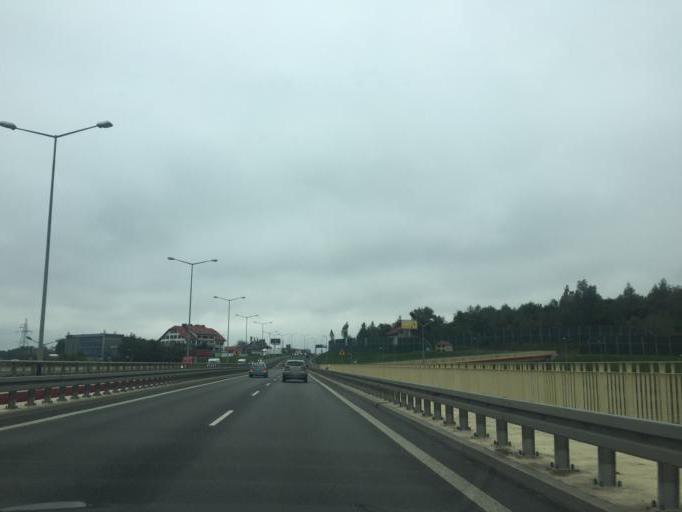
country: PL
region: Lesser Poland Voivodeship
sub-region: Powiat wielicki
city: Czarnochowice
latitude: 50.0053
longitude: 20.0196
